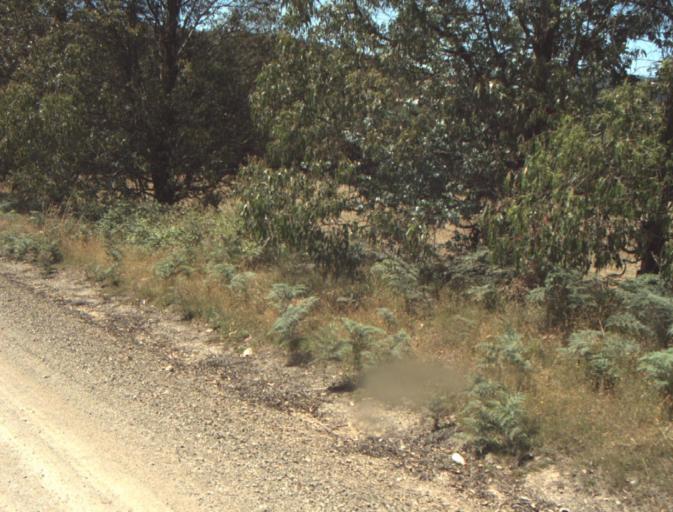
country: AU
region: Tasmania
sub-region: Dorset
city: Scottsdale
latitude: -41.3232
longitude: 147.4457
